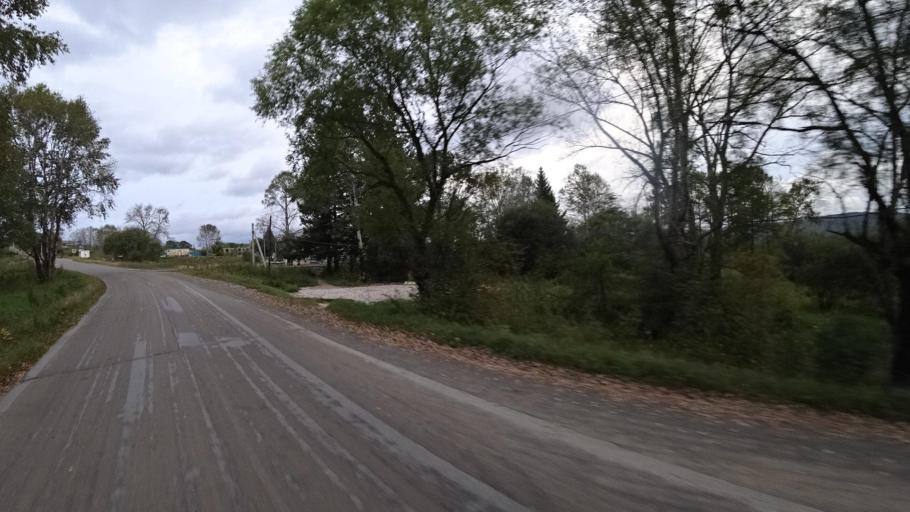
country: RU
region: Jewish Autonomous Oblast
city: Izvestkovyy
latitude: 48.9729
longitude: 131.5809
